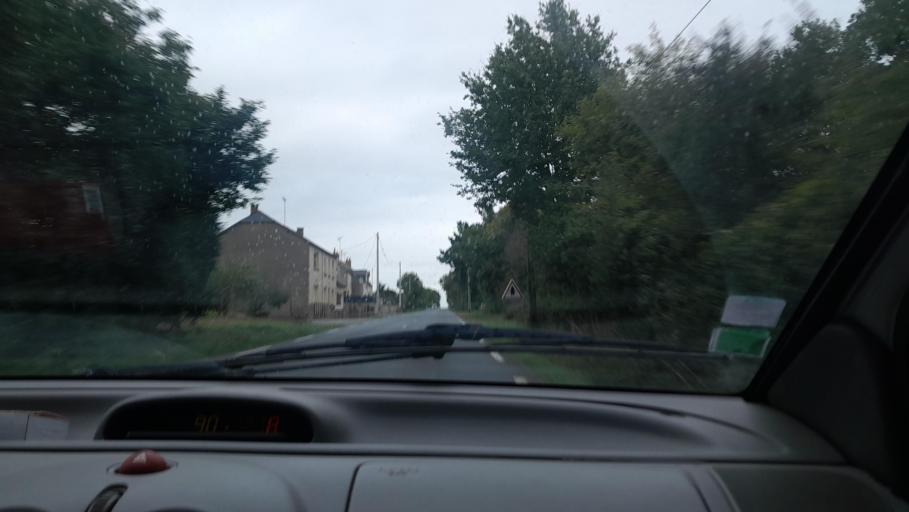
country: FR
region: Pays de la Loire
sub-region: Departement de Maine-et-Loire
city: Pouance
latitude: 47.6658
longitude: -1.1917
